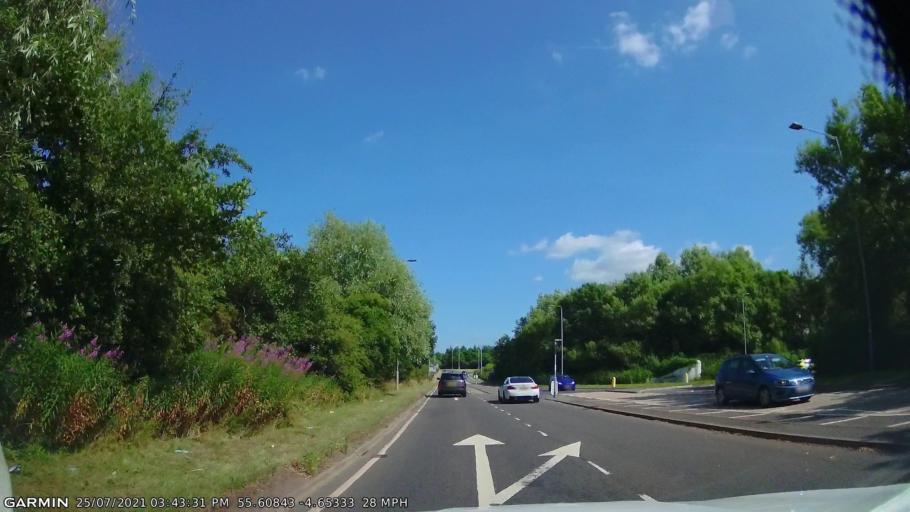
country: GB
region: Scotland
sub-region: North Ayrshire
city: Irvine
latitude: 55.6084
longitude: -4.6533
